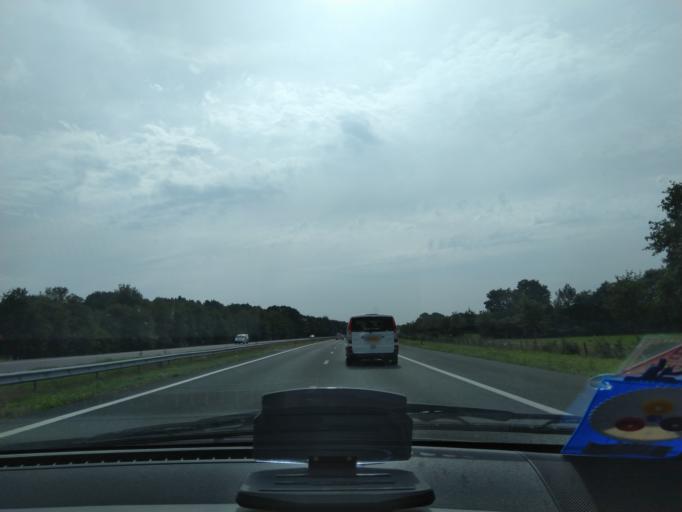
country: NL
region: Drenthe
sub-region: Gemeente Assen
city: Assen
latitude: 52.9027
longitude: 6.5304
